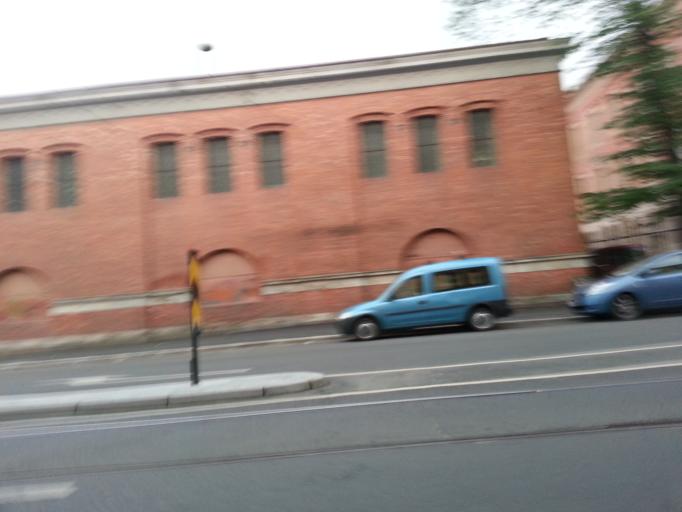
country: NO
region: Oslo
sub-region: Oslo
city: Oslo
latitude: 59.9097
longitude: 10.7490
